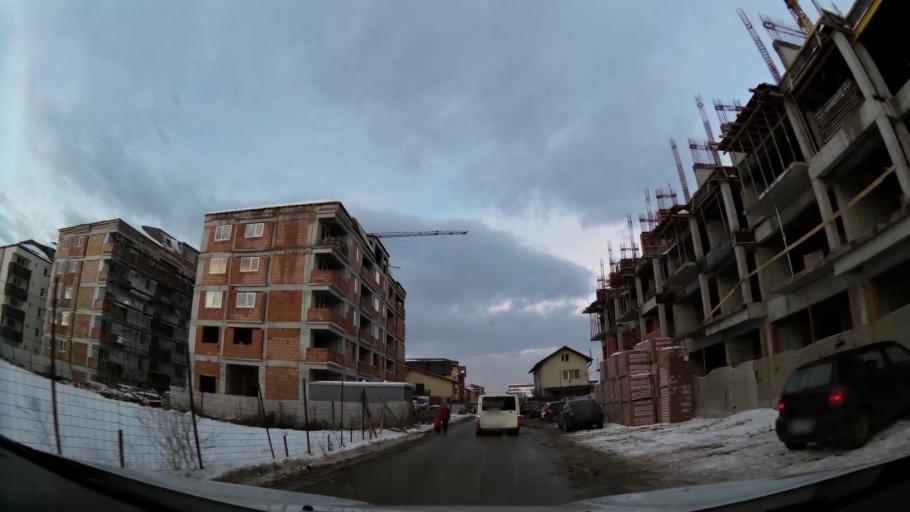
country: RO
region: Ilfov
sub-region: Comuna Popesti-Leordeni
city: Popesti-Leordeni
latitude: 44.3677
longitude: 26.1547
